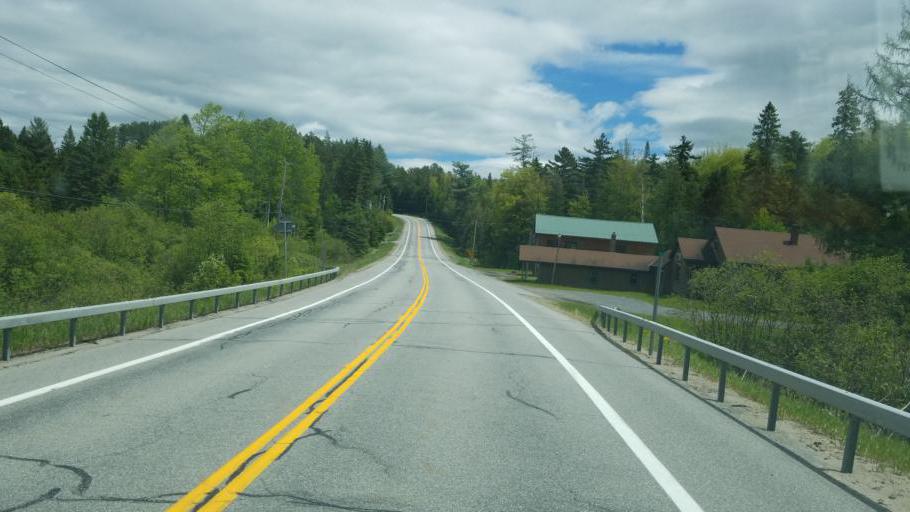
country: US
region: New York
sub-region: Hamilton County
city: Lake Pleasant
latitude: 43.7806
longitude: -74.2985
